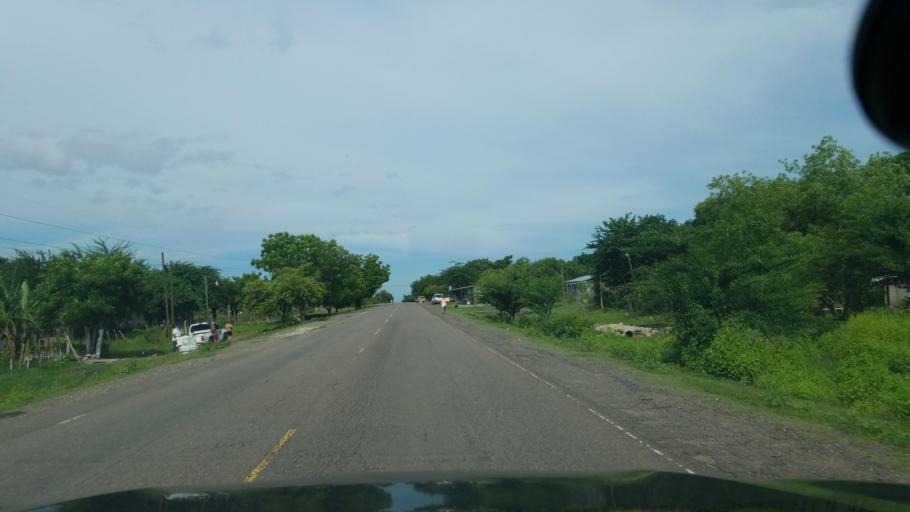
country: HN
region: Choluteca
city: Santa Ana de Yusguare
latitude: 13.3598
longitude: -87.0936
